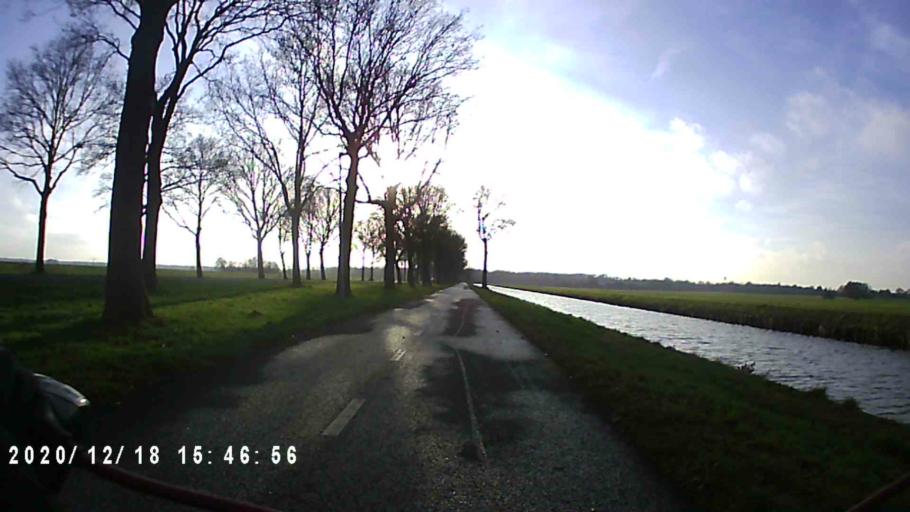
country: NL
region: Drenthe
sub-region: Gemeente Tynaarlo
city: Zuidlaren
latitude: 53.1054
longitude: 6.7043
